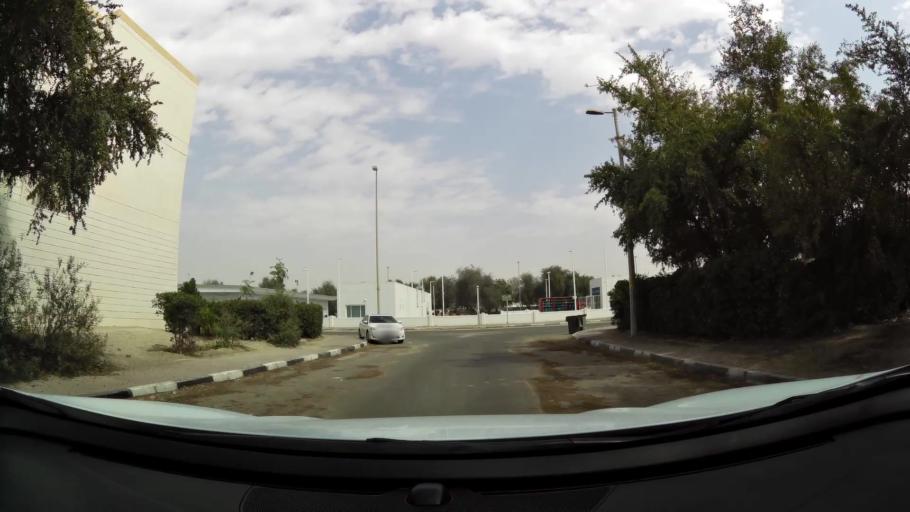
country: AE
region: Abu Dhabi
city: Abu Dhabi
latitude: 24.3028
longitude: 54.6223
